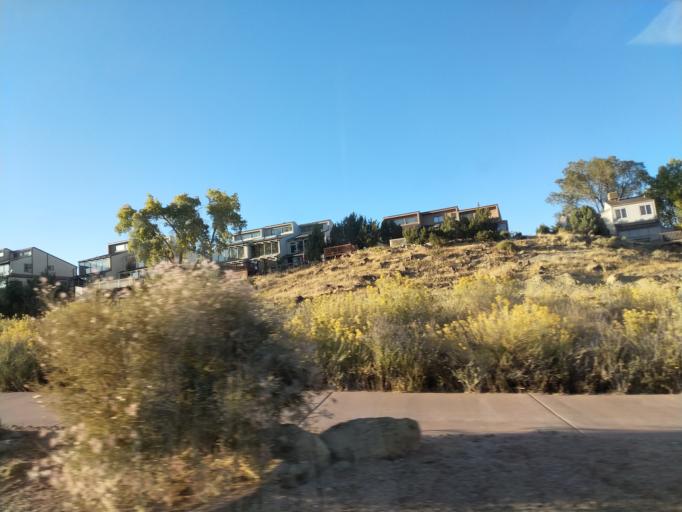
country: US
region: Colorado
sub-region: Mesa County
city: Redlands
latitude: 39.0568
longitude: -108.6181
